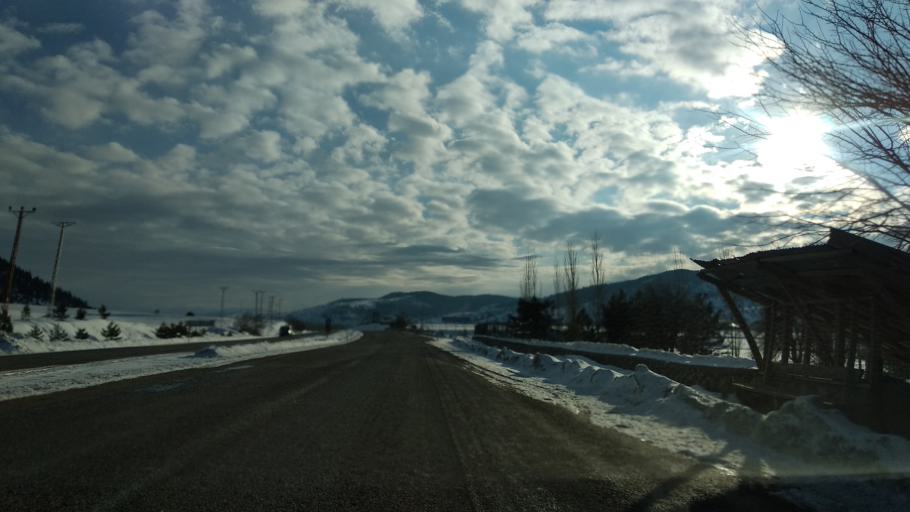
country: TR
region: Kahramanmaras
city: Goksun
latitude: 38.0866
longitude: 36.4677
